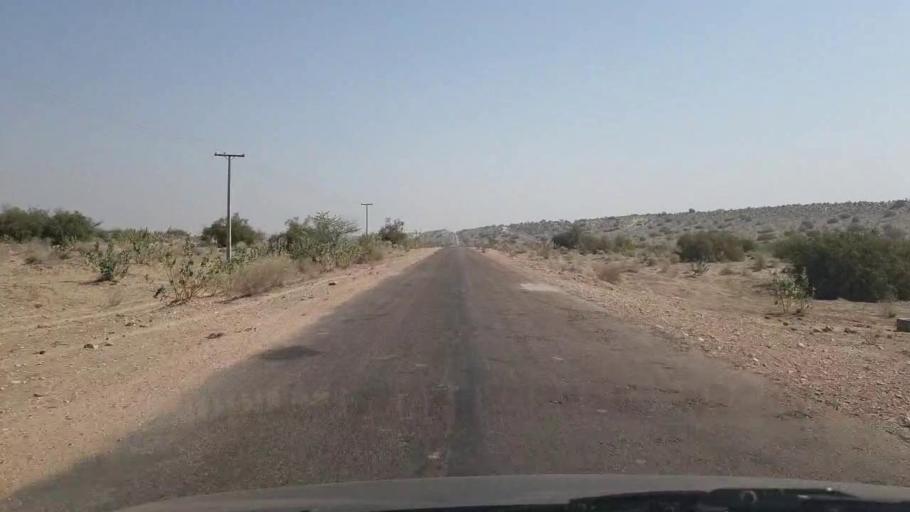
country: PK
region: Sindh
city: Chor
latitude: 25.5759
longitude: 69.9124
